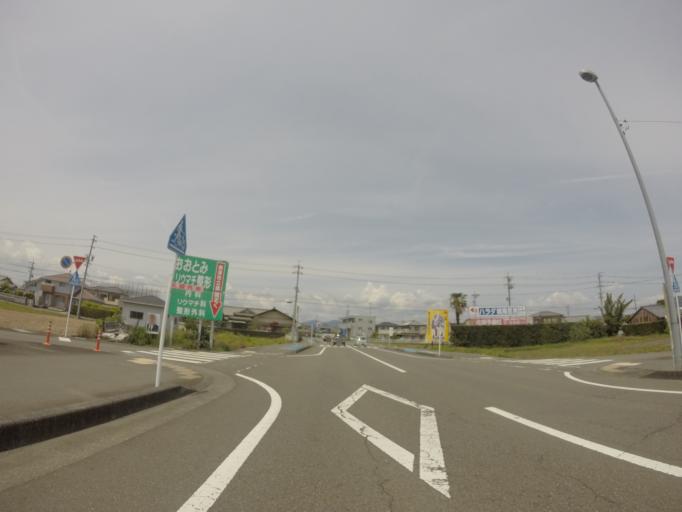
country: JP
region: Shizuoka
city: Fujieda
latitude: 34.8682
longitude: 138.2806
